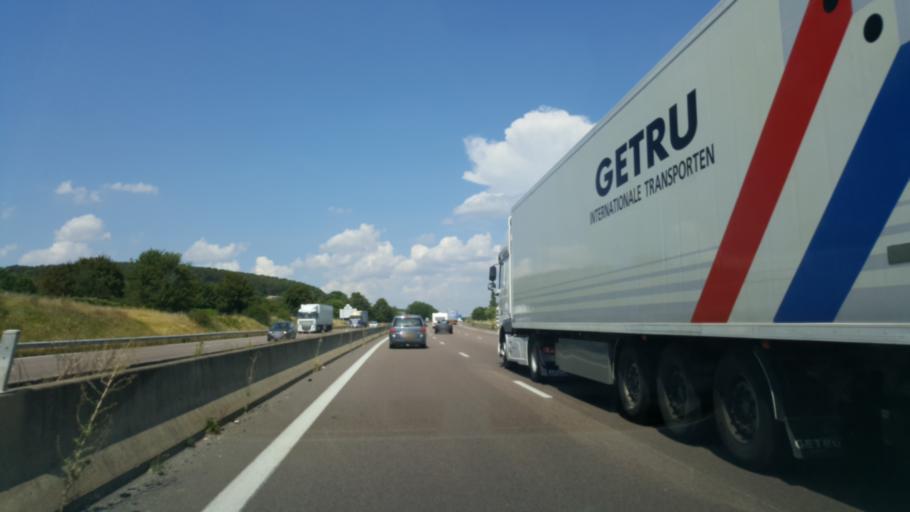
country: FR
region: Bourgogne
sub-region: Departement de Saone-et-Loire
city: Tournus
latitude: 46.5693
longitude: 4.8958
